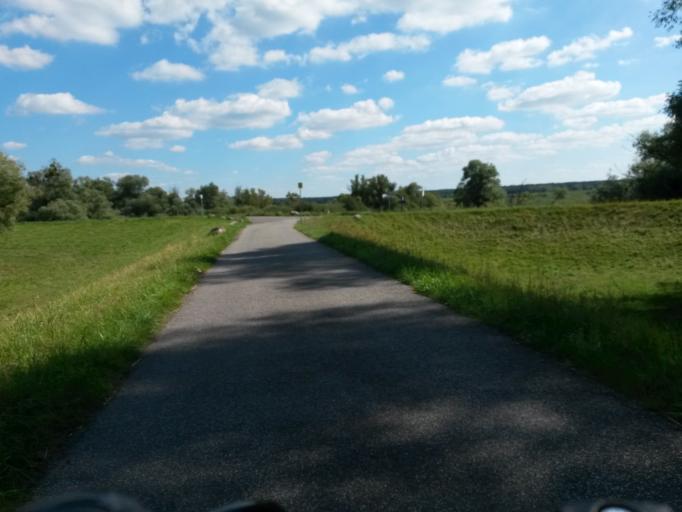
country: DE
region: Brandenburg
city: Schoneberg
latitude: 52.9873
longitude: 14.1765
